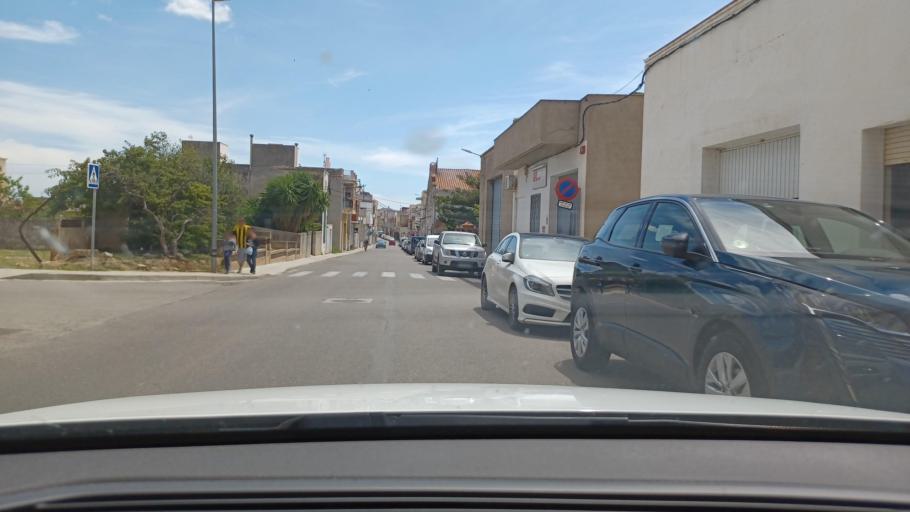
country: ES
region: Valencia
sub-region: Provincia de Castello
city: Rosell
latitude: 40.6375
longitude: 0.2809
